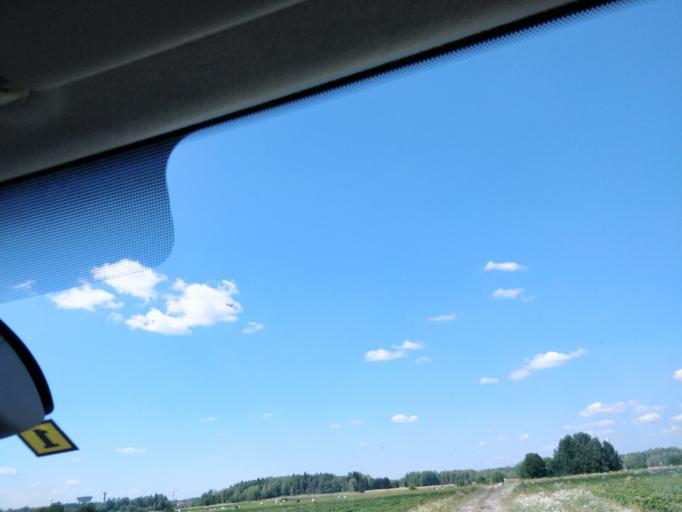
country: FI
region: Uusimaa
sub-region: Helsinki
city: Vantaa
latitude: 60.3076
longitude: 25.0742
